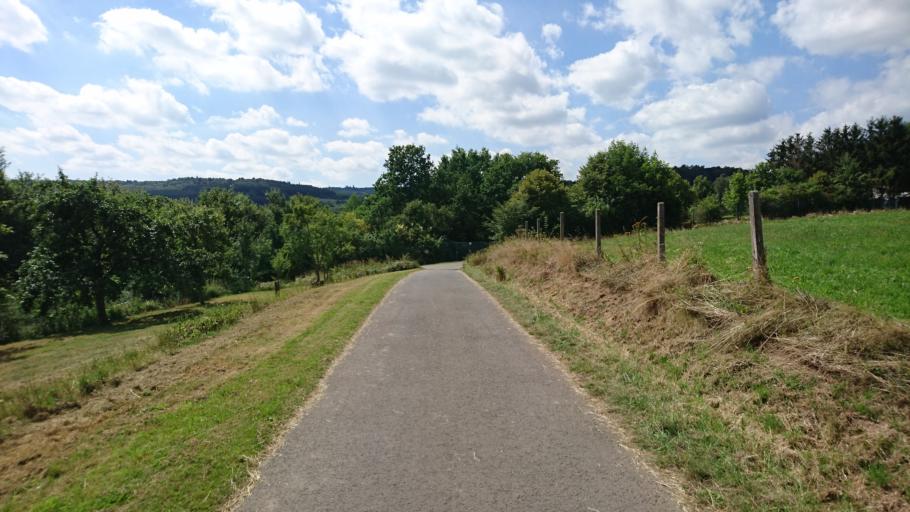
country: DE
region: Hesse
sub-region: Regierungsbezirk Giessen
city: Breitscheid
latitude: 50.6743
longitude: 8.2265
